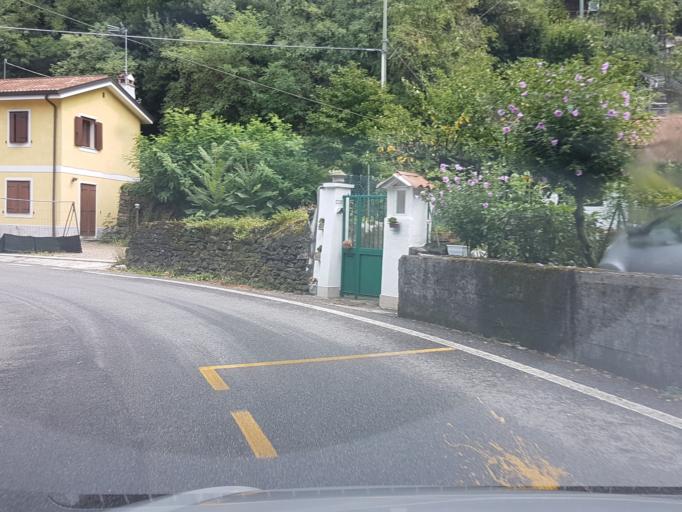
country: IT
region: Friuli Venezia Giulia
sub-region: Provincia di Trieste
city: Villa Opicina
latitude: 45.6771
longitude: 13.7614
